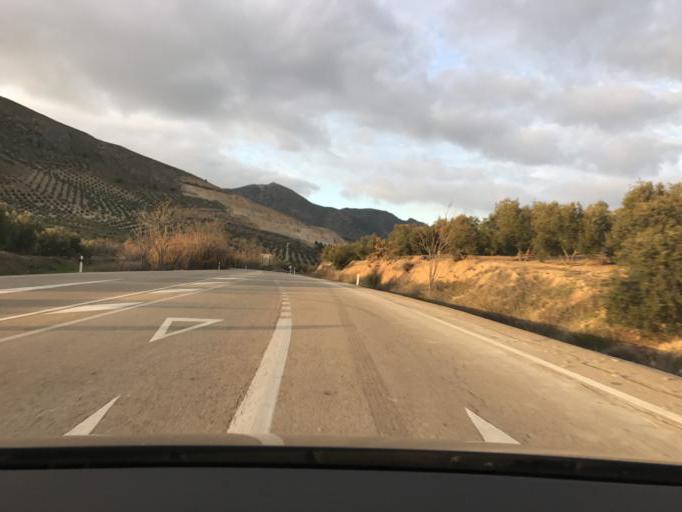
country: ES
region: Andalusia
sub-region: Provincia de Jaen
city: Jodar
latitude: 37.8140
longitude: -3.3699
